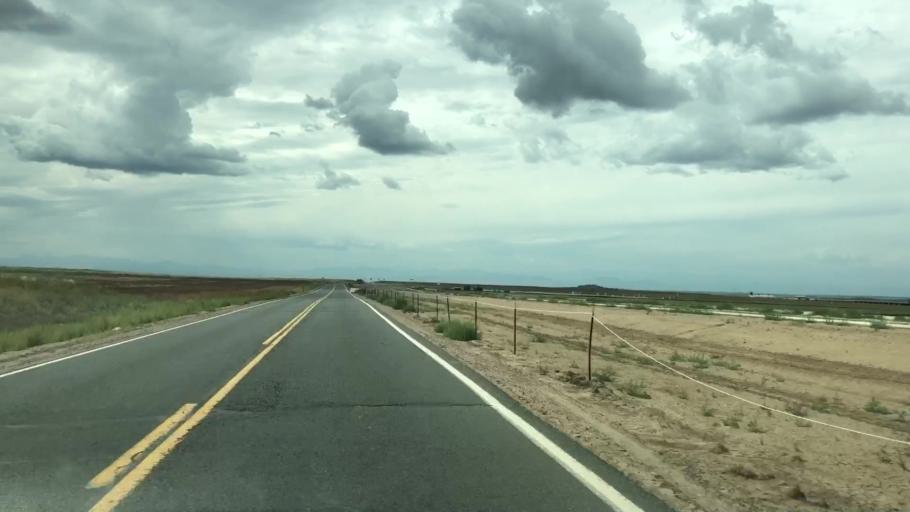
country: US
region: Colorado
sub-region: Adams County
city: Aurora
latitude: 39.7981
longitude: -104.6737
